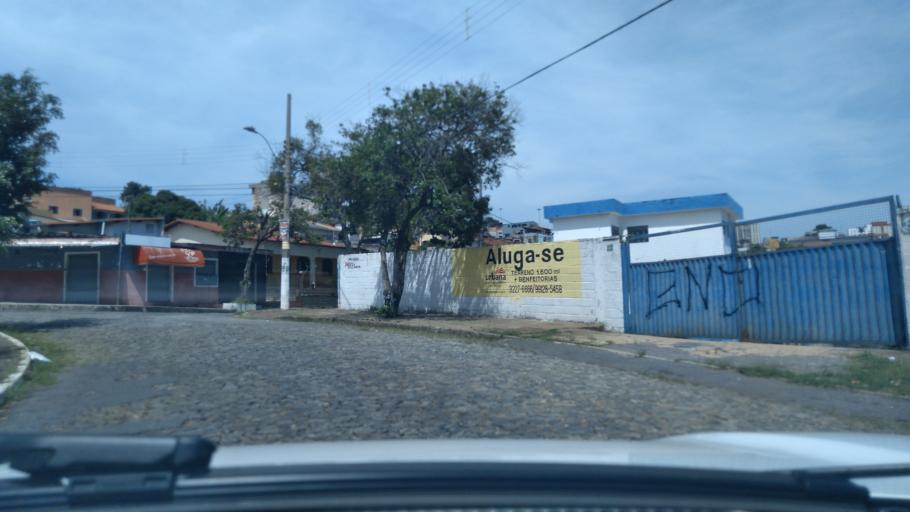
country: BR
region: Minas Gerais
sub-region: Contagem
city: Contagem
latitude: -19.9269
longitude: -44.0016
